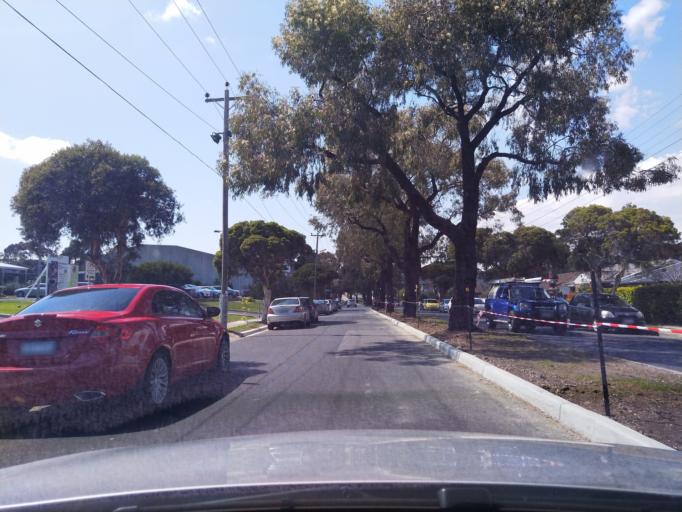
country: AU
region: Victoria
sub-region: Banyule
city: Bellfield
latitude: -37.7568
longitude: 145.0421
